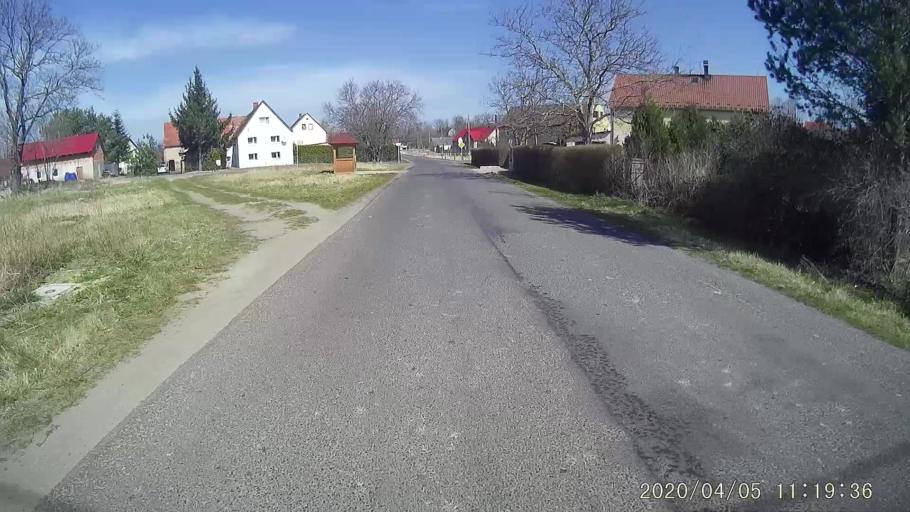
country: PL
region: Lower Silesian Voivodeship
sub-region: Powiat zgorzelecki
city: Sulikow
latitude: 51.0568
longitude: 15.1089
